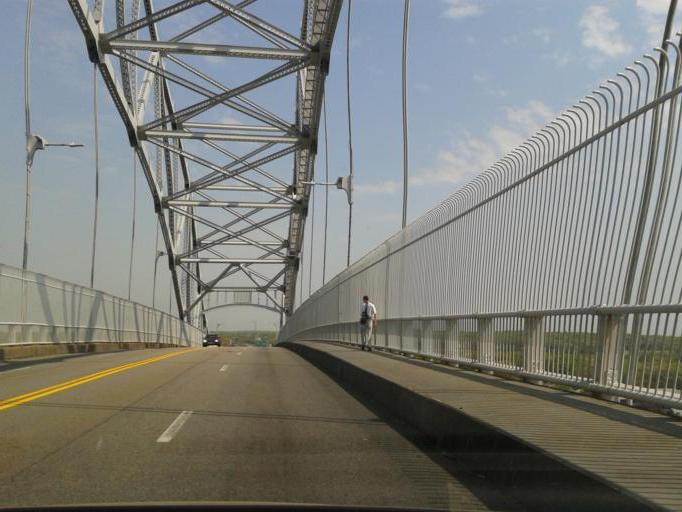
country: US
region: Massachusetts
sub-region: Barnstable County
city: Sagamore
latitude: 41.7759
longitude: -70.5433
